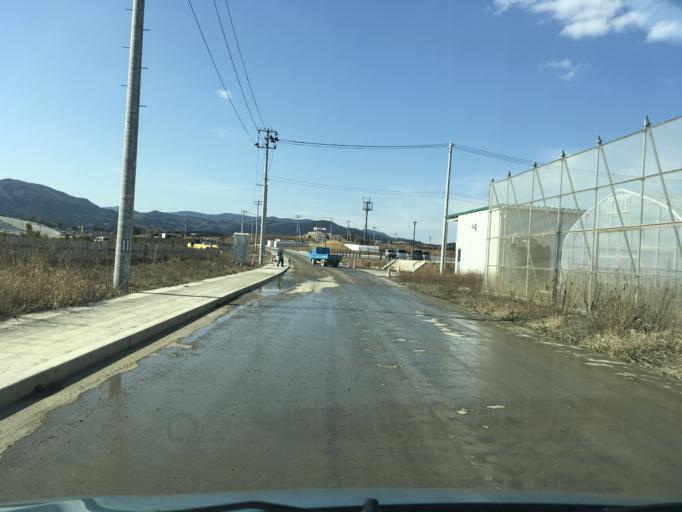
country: JP
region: Iwate
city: Ofunato
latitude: 38.8252
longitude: 141.5899
